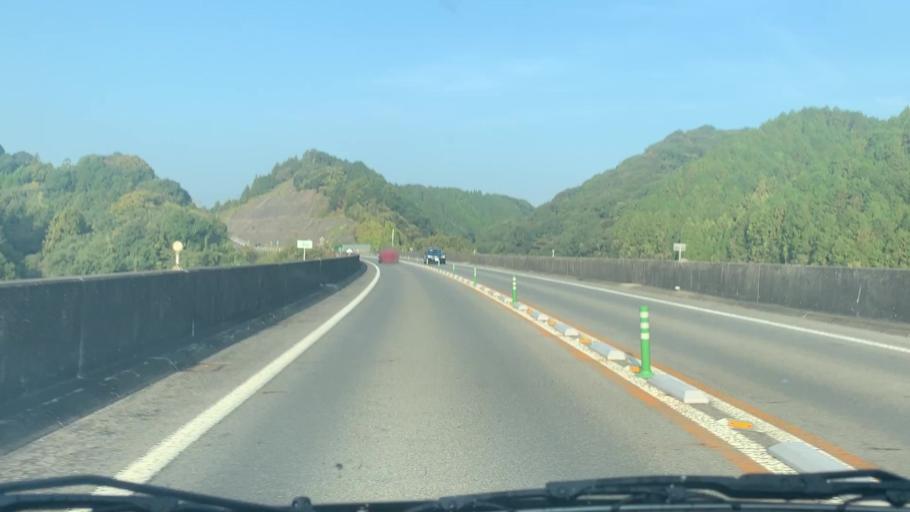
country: JP
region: Saga Prefecture
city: Ureshinomachi-shimojuku
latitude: 33.1467
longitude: 129.9495
